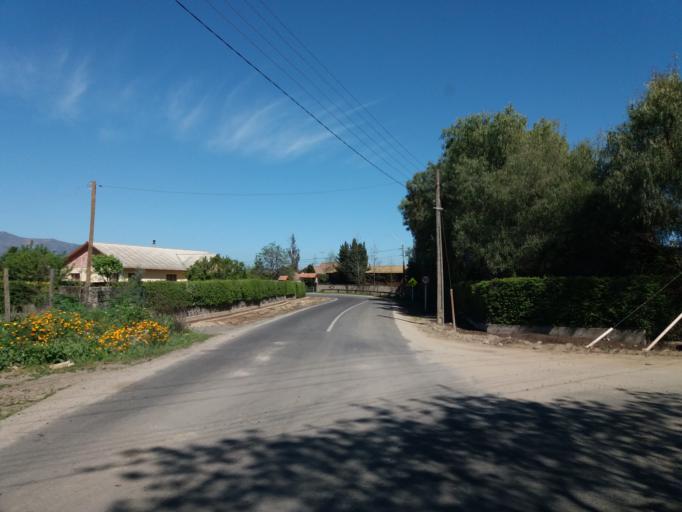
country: CL
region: Valparaiso
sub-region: Provincia de Marga Marga
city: Limache
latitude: -33.0016
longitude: -71.1847
